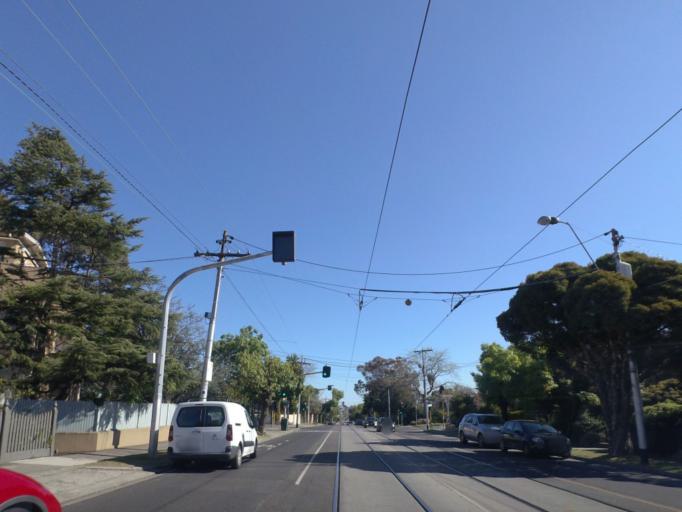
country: AU
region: Victoria
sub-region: Boroondara
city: Kew
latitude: -37.8098
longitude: 145.0267
